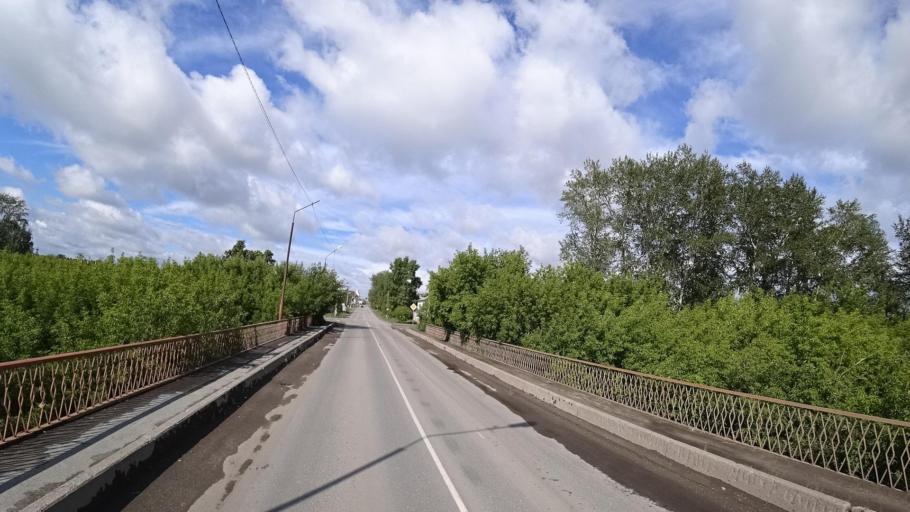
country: RU
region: Sverdlovsk
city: Kamyshlov
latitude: 56.8400
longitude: 62.7031
